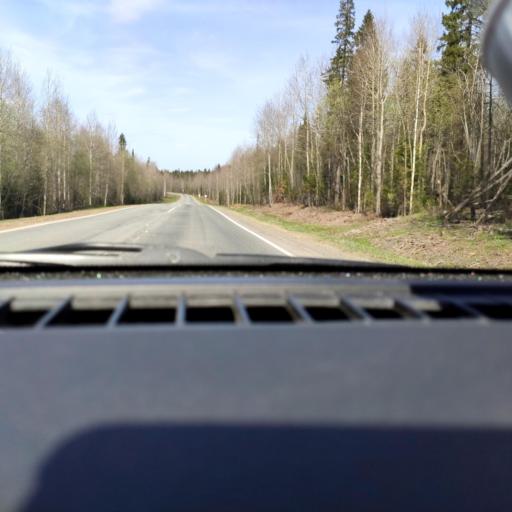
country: RU
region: Perm
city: Polazna
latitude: 58.2591
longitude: 56.1656
